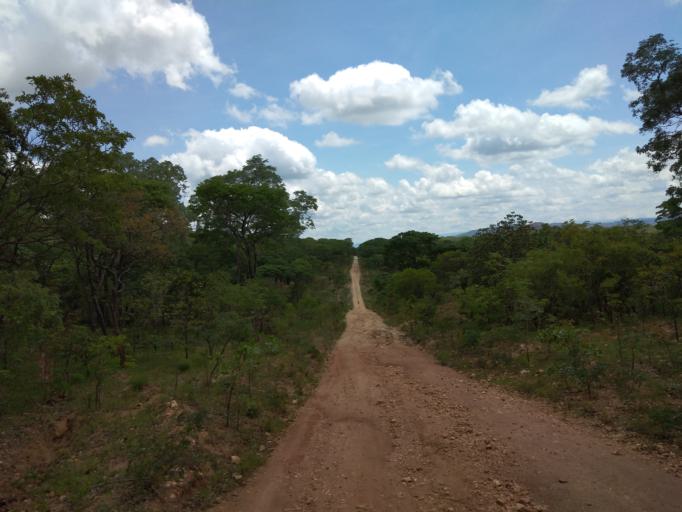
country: ZM
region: Central
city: Mkushi
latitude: -14.0381
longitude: 29.9645
